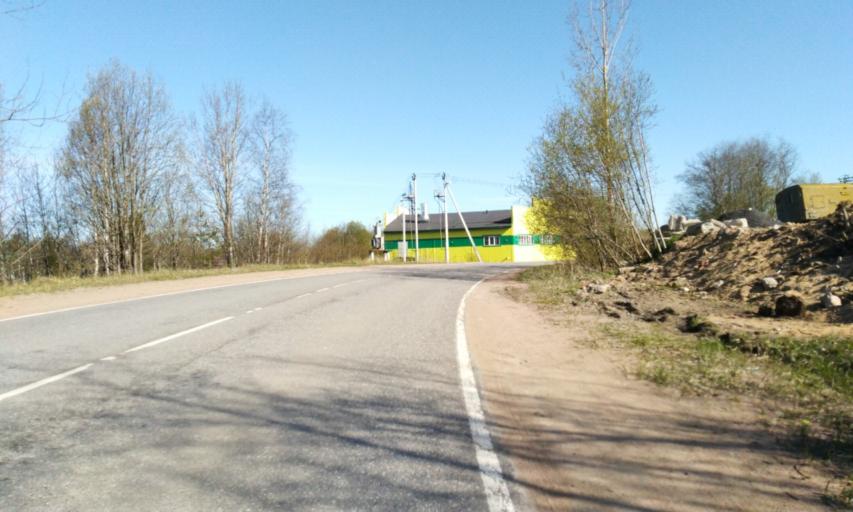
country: RU
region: Leningrad
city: Leskolovo
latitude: 60.3282
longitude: 30.4244
